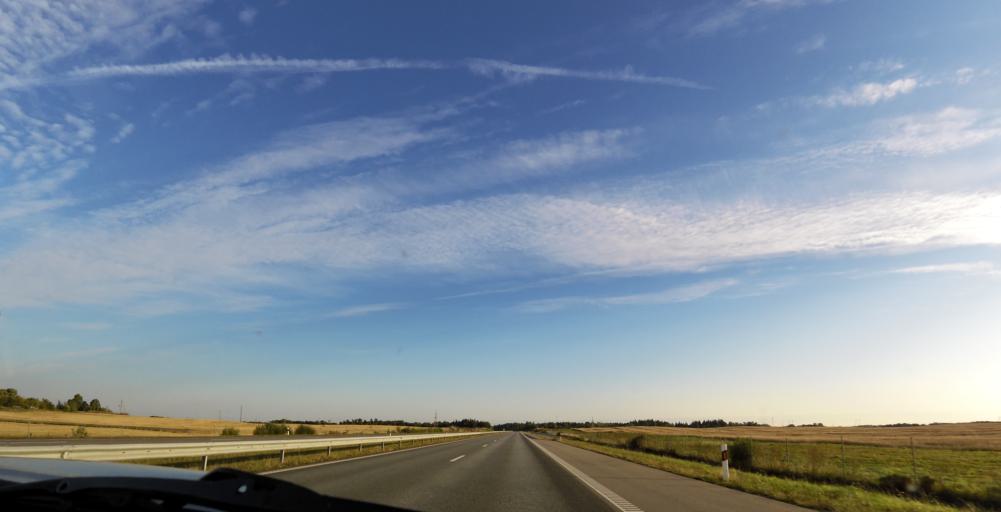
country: LT
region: Vilnius County
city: Ukmerge
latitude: 55.1986
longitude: 24.8147
